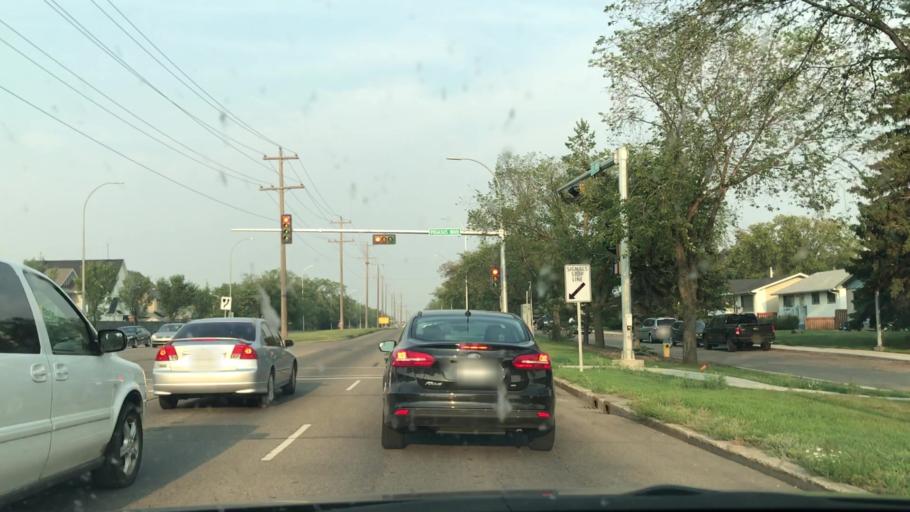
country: CA
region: Alberta
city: Edmonton
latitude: 53.5994
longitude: -113.5048
